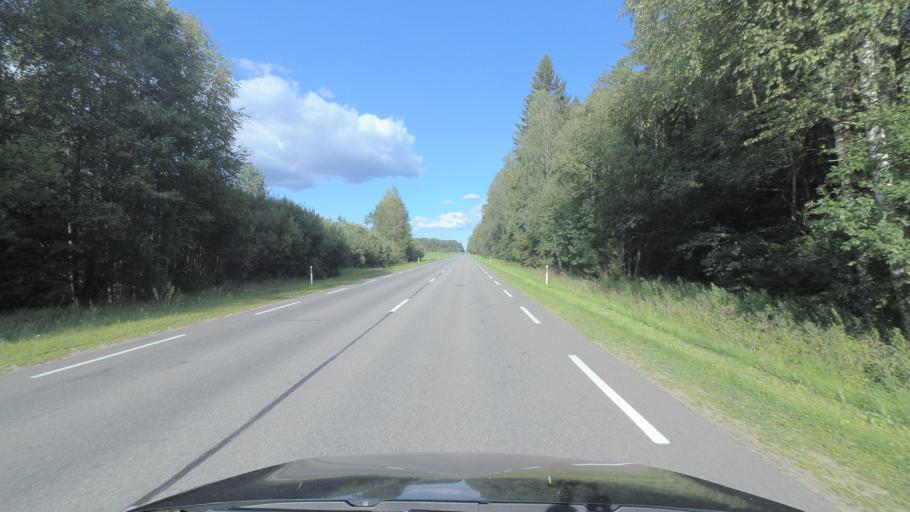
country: LT
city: Pabrade
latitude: 54.9603
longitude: 25.6941
